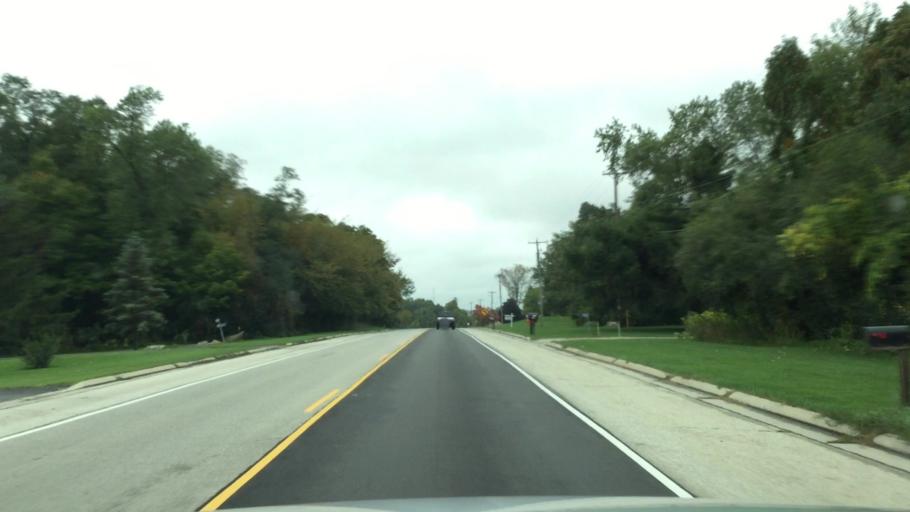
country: US
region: Wisconsin
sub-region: Racine County
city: Eagle Lake
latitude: 42.7423
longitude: -88.0805
